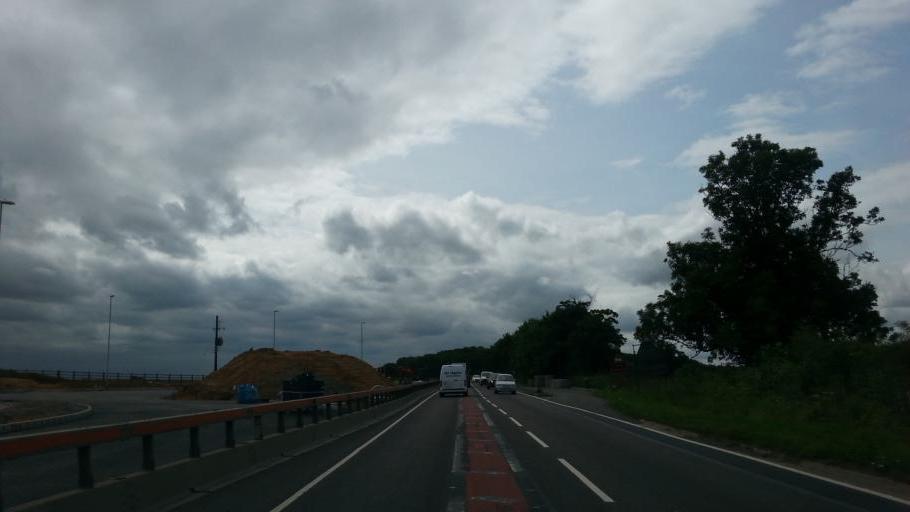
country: GB
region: England
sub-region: Northamptonshire
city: Northampton
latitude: 52.2969
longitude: -0.8315
